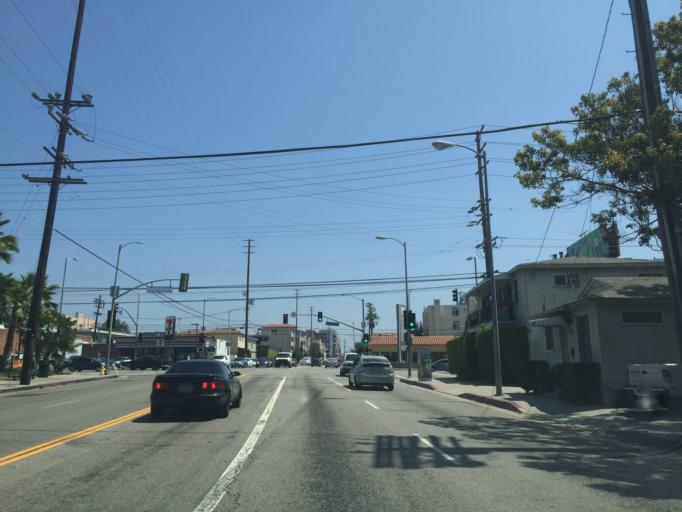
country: US
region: California
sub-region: Los Angeles County
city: Culver City
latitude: 34.0243
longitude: -118.4122
